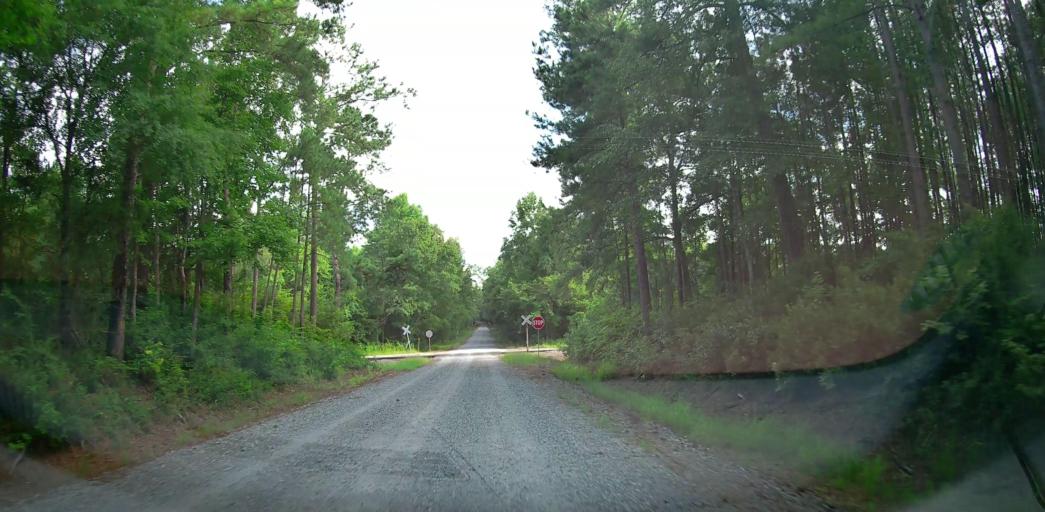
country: US
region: Georgia
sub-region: Bleckley County
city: Cochran
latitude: 32.4307
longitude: -83.4537
